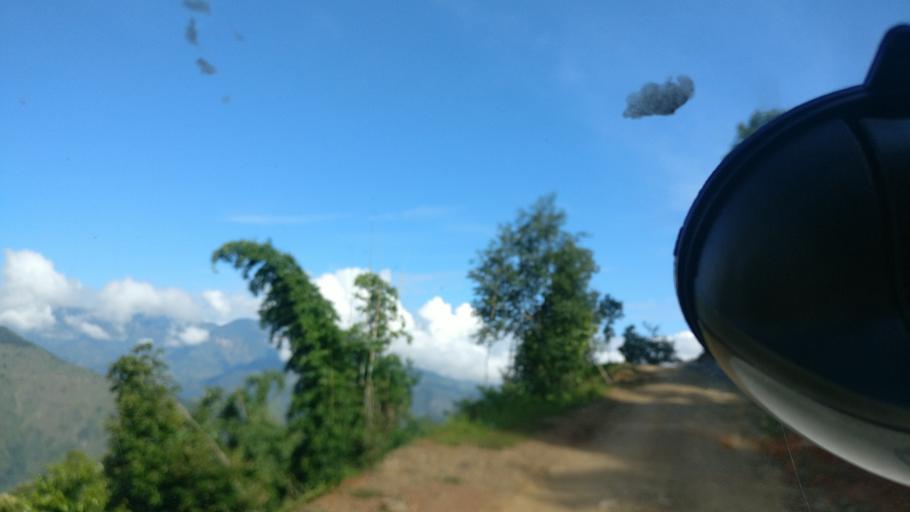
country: NP
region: Western Region
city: Baglung
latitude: 28.1396
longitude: 83.6491
